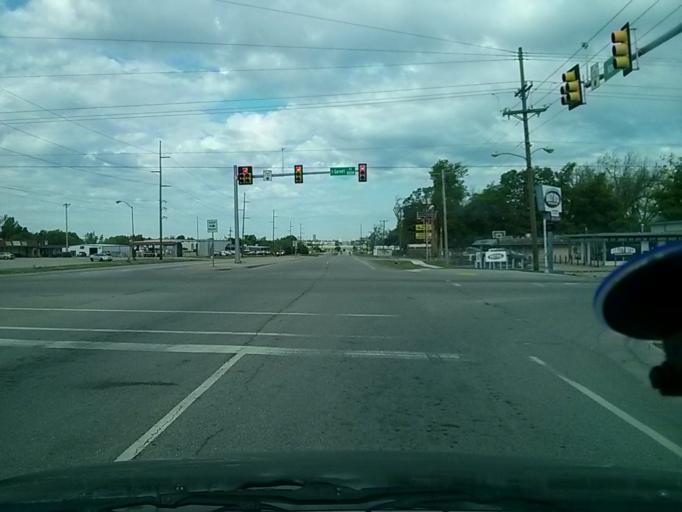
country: US
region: Oklahoma
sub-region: Rogers County
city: Catoosa
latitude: 36.1607
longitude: -95.8509
